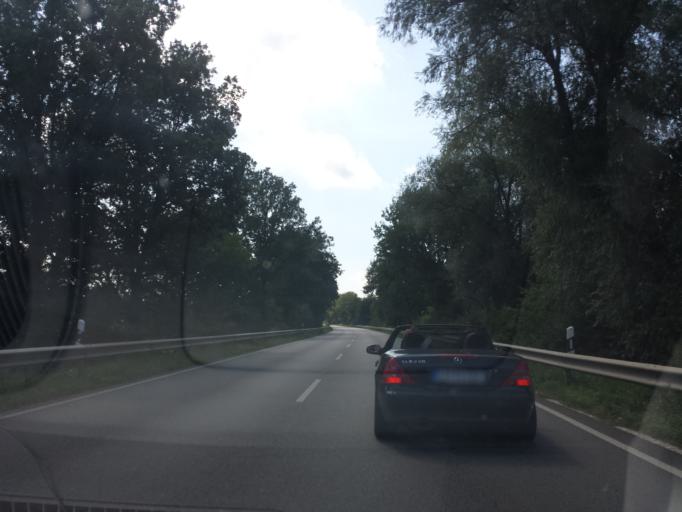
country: DE
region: Bavaria
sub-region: Lower Bavaria
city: Abensberg
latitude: 48.7968
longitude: 11.8302
